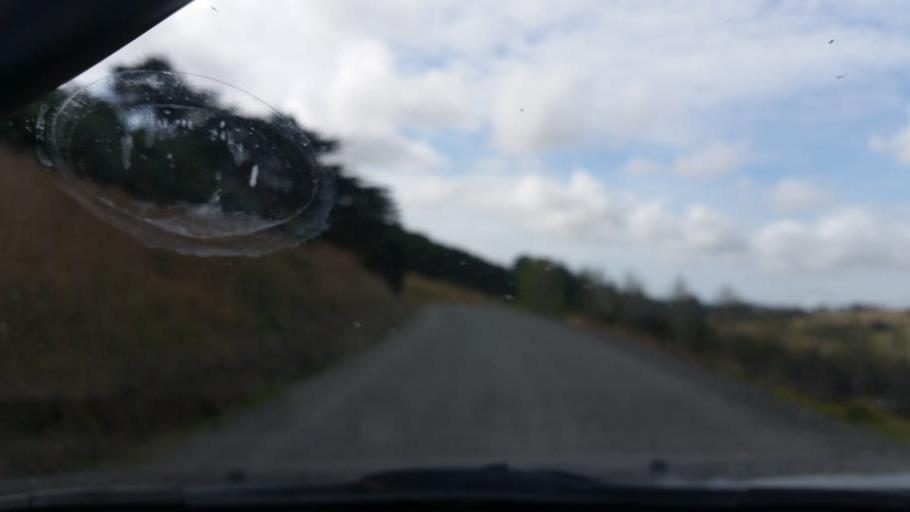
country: NZ
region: Northland
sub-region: Kaipara District
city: Dargaville
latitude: -35.9758
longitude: 173.9517
